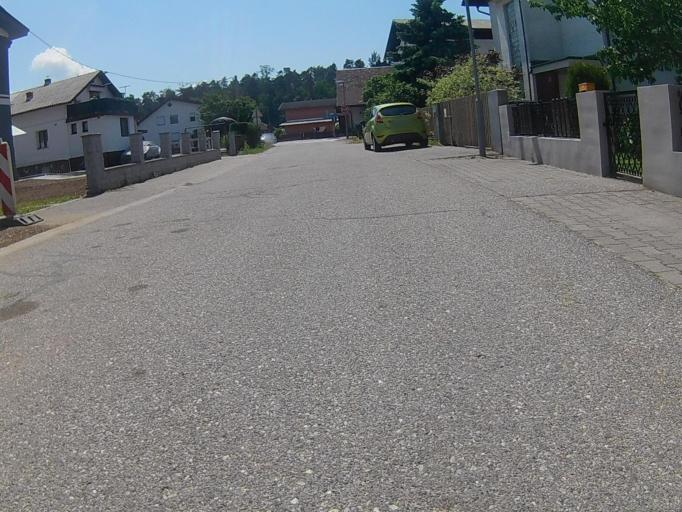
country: SI
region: Miklavz na Dravskem Polju
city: Miklavz na Dravskem Polju
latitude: 46.5021
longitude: 15.6986
